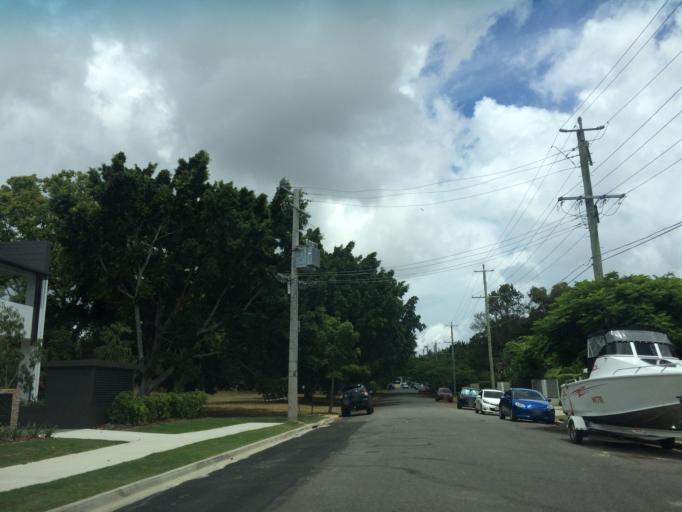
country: AU
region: Queensland
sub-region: Brisbane
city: Ascot
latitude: -27.4444
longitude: 153.0578
